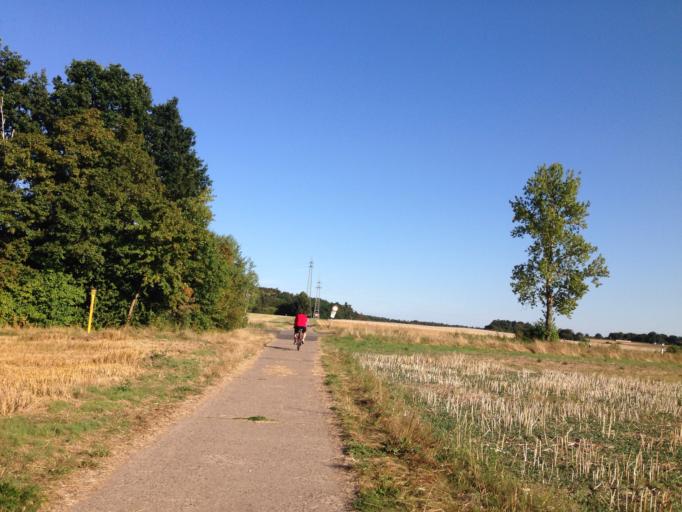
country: DE
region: Hesse
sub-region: Regierungsbezirk Giessen
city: Lich
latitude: 50.5318
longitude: 8.7562
